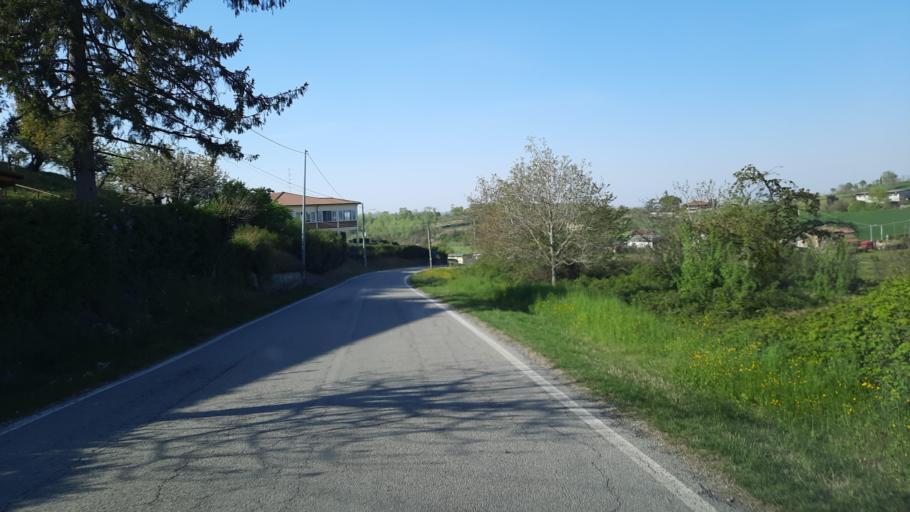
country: IT
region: Piedmont
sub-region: Provincia di Alessandria
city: Camagna Monferrato
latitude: 45.0198
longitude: 8.4350
